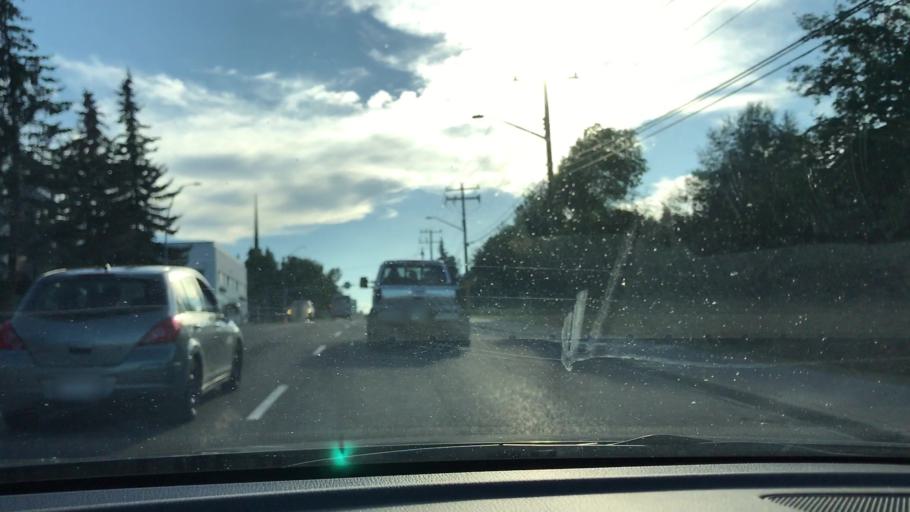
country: CA
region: Alberta
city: Calgary
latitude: 51.0378
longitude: -114.1046
